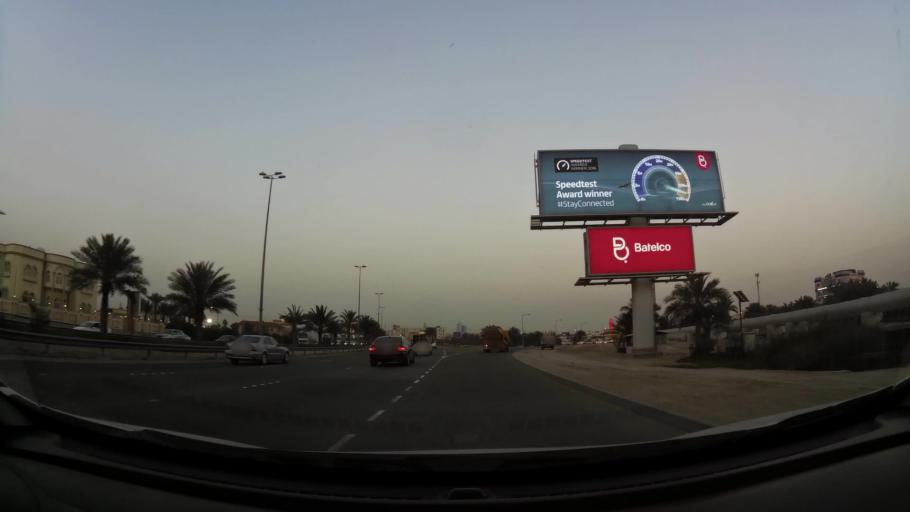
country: BH
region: Manama
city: Jidd Hafs
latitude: 26.1982
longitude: 50.5545
